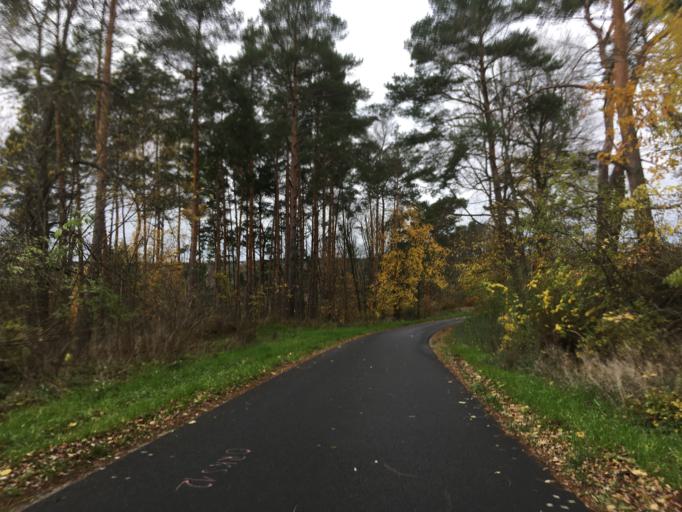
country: DE
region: Brandenburg
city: Jamlitz
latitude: 52.0868
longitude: 14.4364
